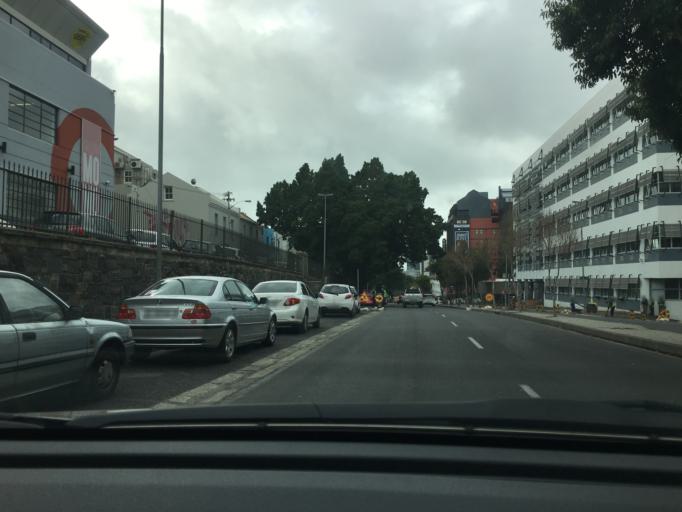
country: ZA
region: Western Cape
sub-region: City of Cape Town
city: Cape Town
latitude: -33.9238
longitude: 18.4138
